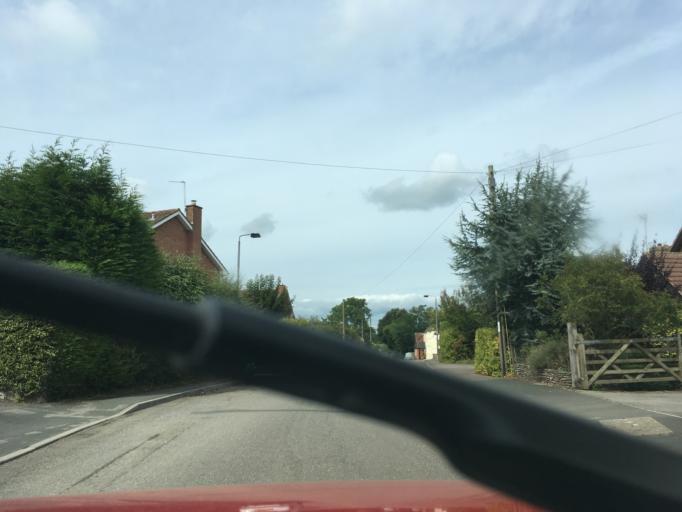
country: GB
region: England
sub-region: South Gloucestershire
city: Charfield
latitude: 51.6313
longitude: -2.4008
